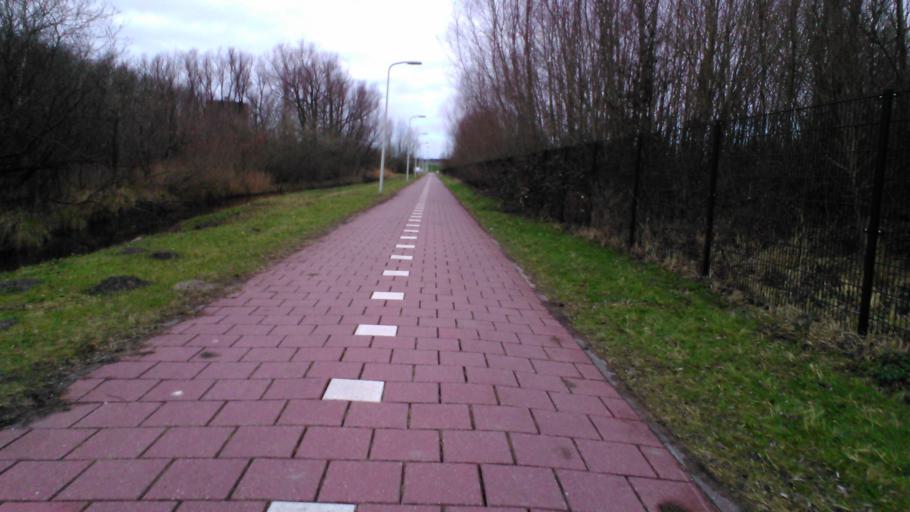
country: NL
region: South Holland
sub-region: Gemeente Den Haag
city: Ypenburg
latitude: 52.0559
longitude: 4.3761
